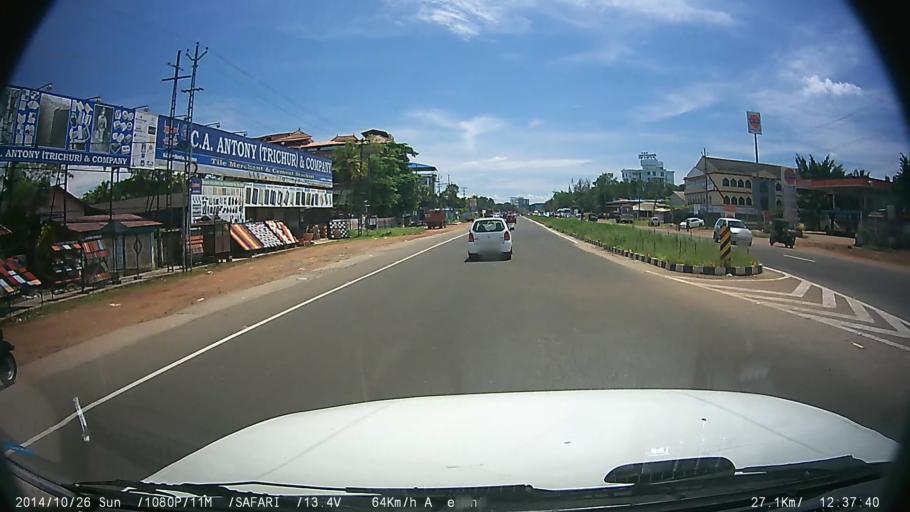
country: IN
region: Kerala
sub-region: Kottayam
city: Kottayam
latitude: 9.5748
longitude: 76.5195
